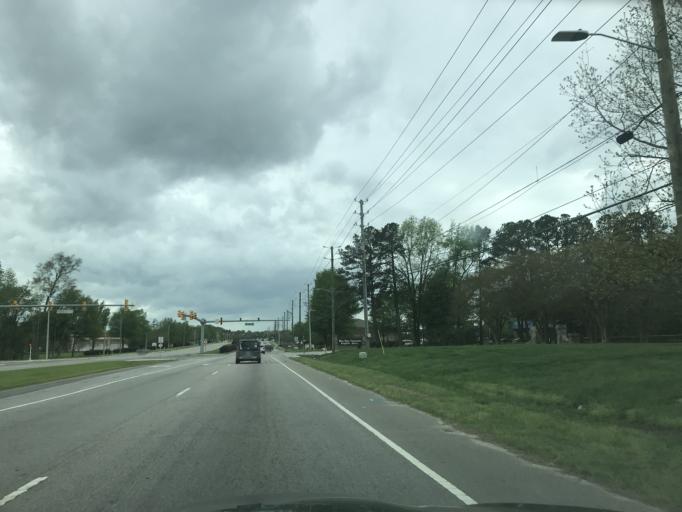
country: US
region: North Carolina
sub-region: Wake County
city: Knightdale
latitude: 35.7982
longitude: -78.5004
